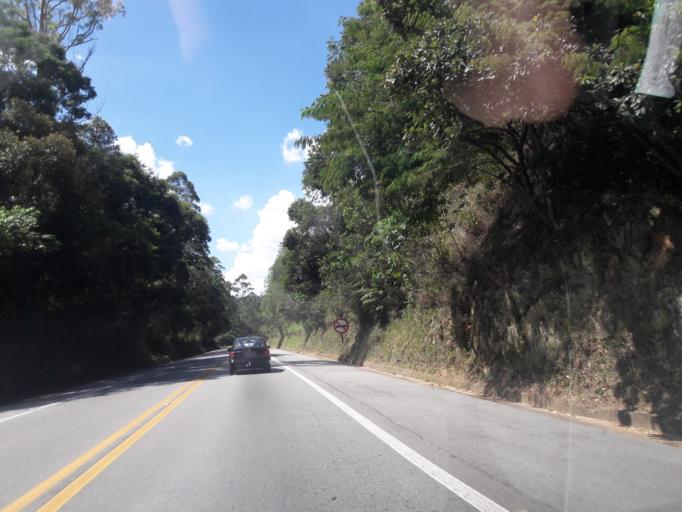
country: BR
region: Sao Paulo
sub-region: Francisco Morato
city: Francisco Morato
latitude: -23.2805
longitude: -46.7958
